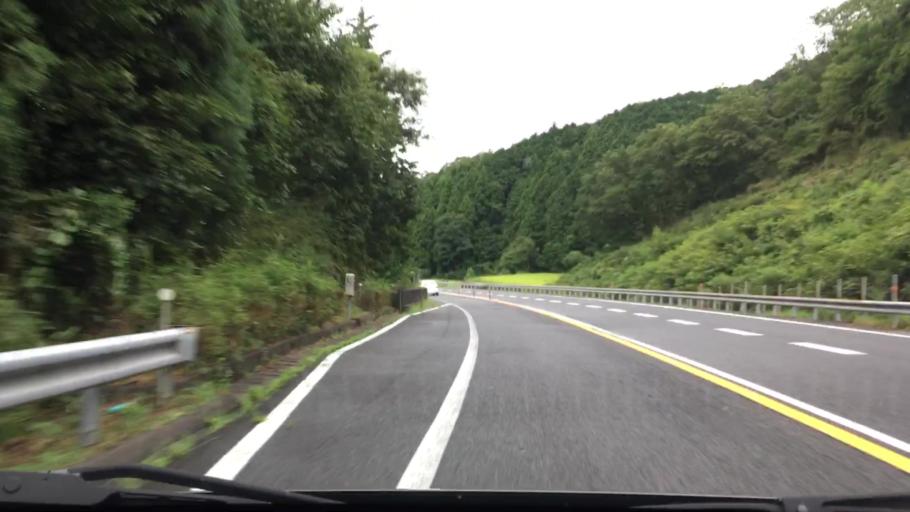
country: JP
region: Hyogo
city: Nishiwaki
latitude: 35.0948
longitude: 134.7758
